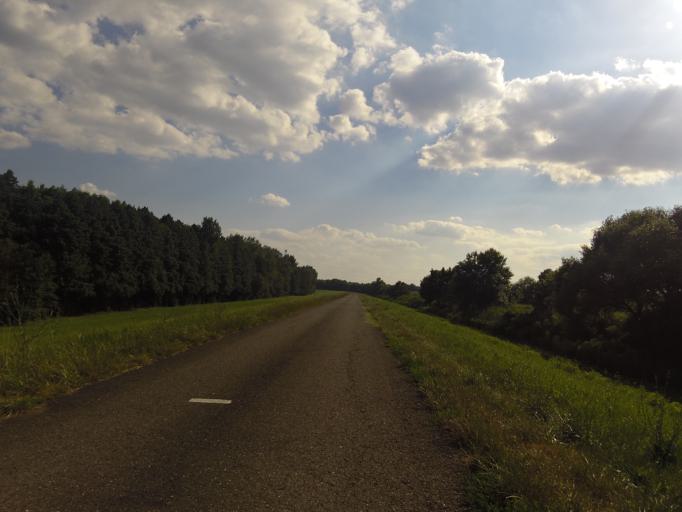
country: HU
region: Jasz-Nagykun-Szolnok
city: Abadszalok
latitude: 47.5195
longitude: 20.5922
